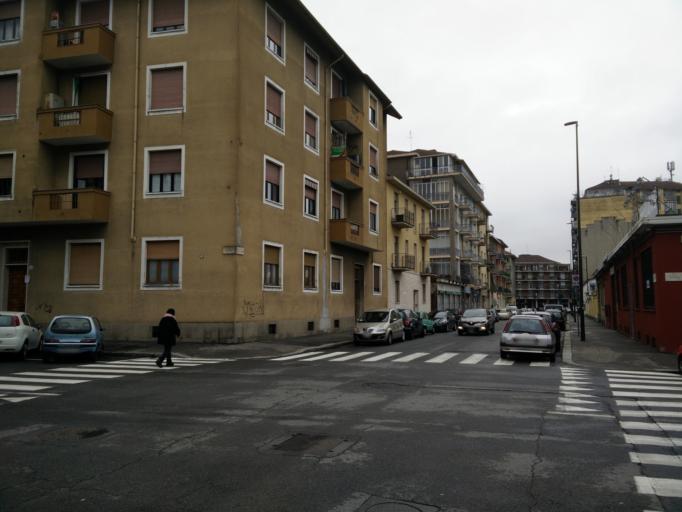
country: IT
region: Piedmont
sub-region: Provincia di Torino
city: Nichelino
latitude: 45.0189
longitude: 7.6538
